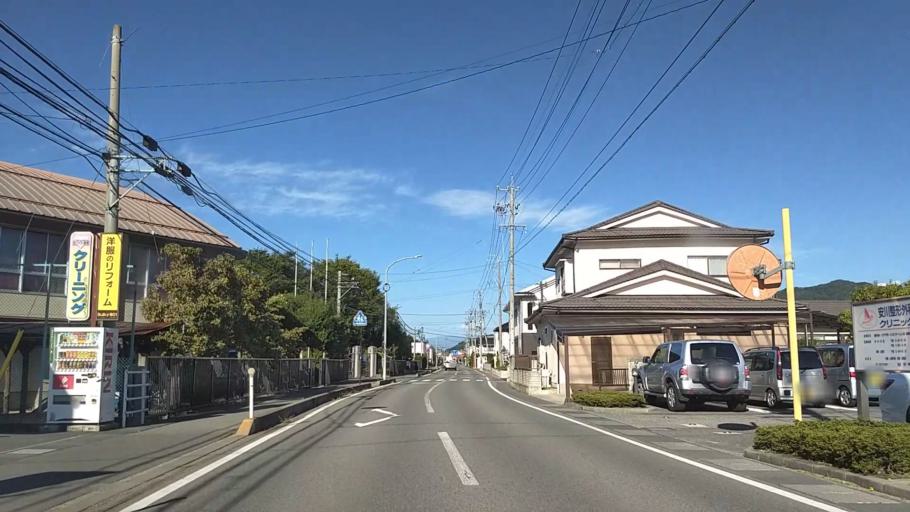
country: JP
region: Nagano
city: Nagano-shi
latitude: 36.5437
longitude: 138.1334
